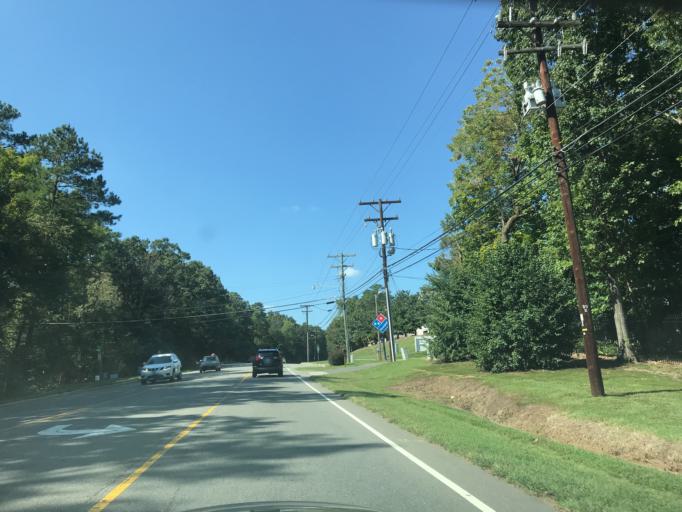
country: US
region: North Carolina
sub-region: Durham County
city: Durham
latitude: 35.9027
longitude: -78.9057
